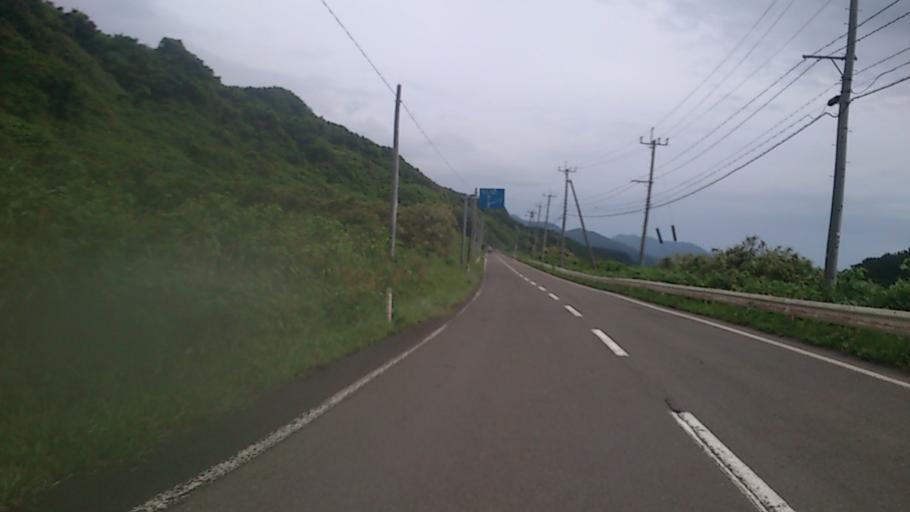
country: JP
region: Akita
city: Noshiromachi
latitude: 40.5257
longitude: 139.9494
